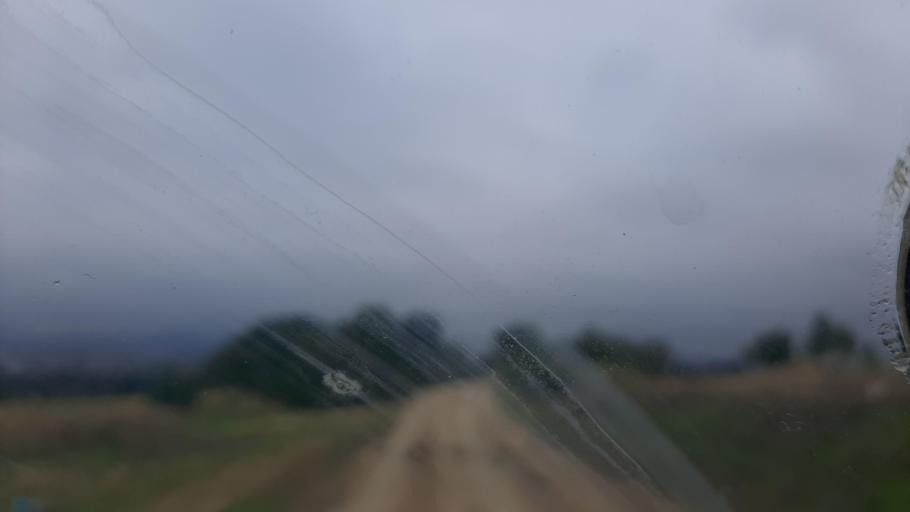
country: TN
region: Tunis
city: La Sebala du Mornag
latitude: 36.5745
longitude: 10.2930
